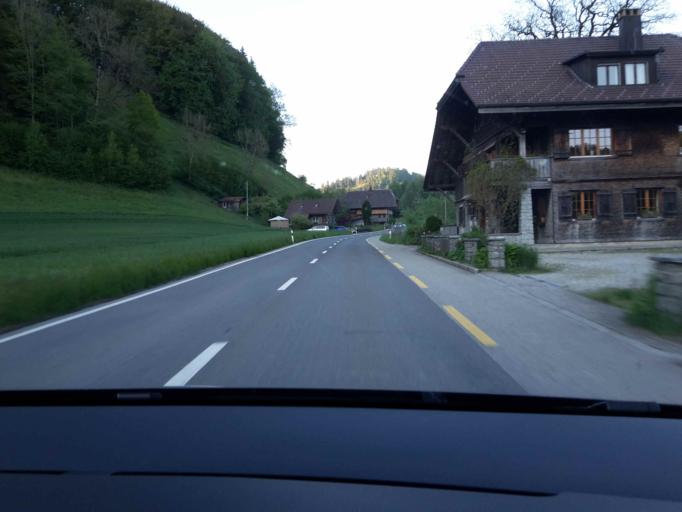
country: CH
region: Bern
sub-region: Emmental District
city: Lutzelfluh
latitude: 47.0281
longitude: 7.6809
